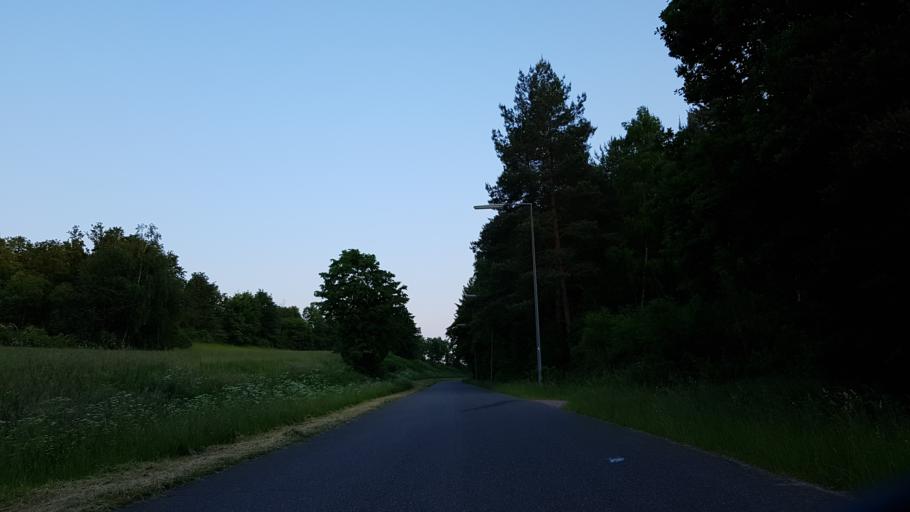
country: DE
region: Lower Saxony
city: Scharnebeck
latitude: 53.2902
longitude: 10.4859
